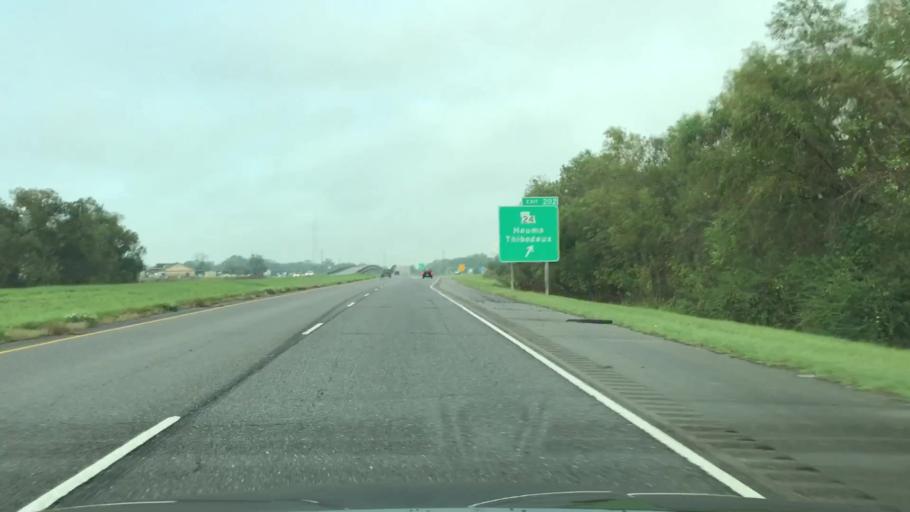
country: US
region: Louisiana
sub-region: Terrebonne Parish
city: Gray
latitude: 29.6805
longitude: -90.7760
